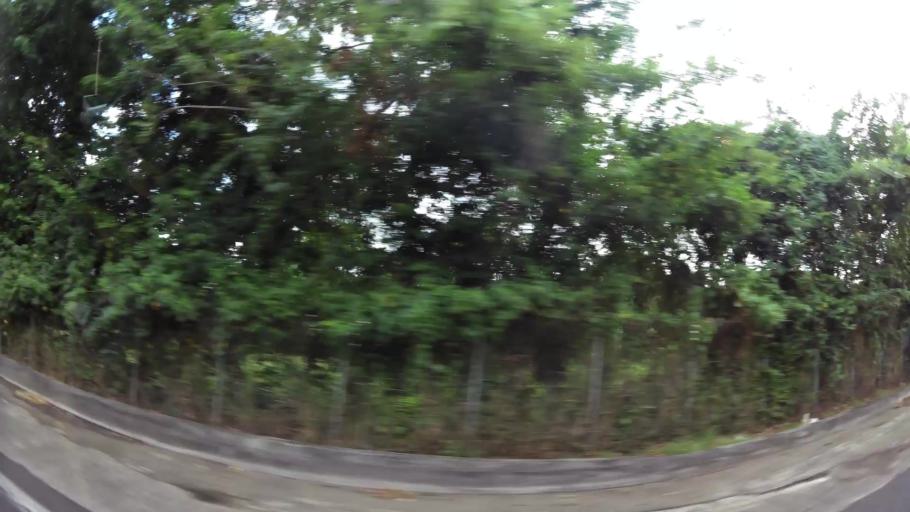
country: MQ
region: Martinique
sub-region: Martinique
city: Ducos
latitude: 14.5224
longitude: -60.9831
